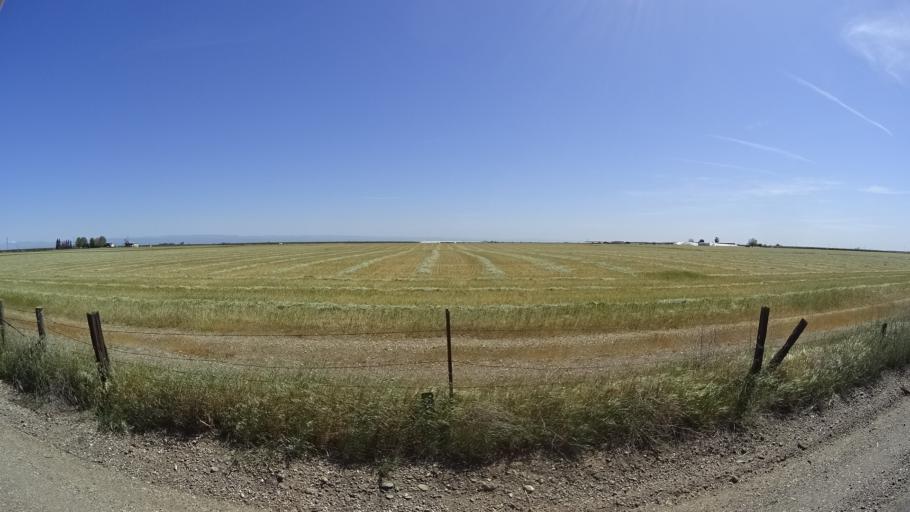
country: US
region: California
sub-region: Glenn County
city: Orland
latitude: 39.6593
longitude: -122.1784
